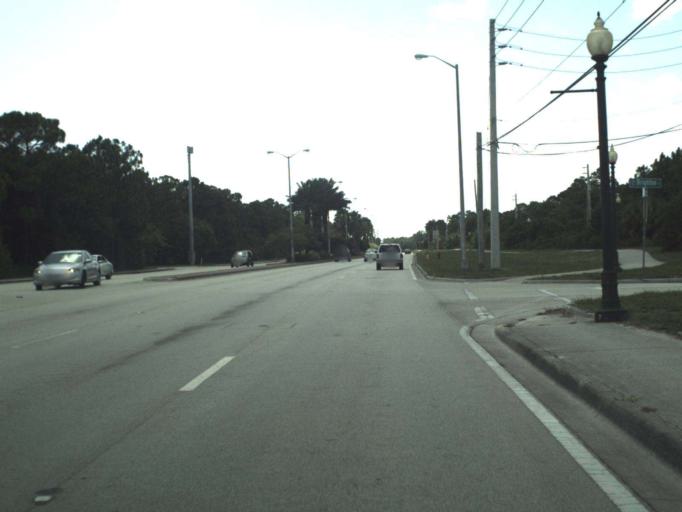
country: US
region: Florida
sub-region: Saint Lucie County
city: Port Saint Lucie
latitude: 27.2589
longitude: -80.3764
